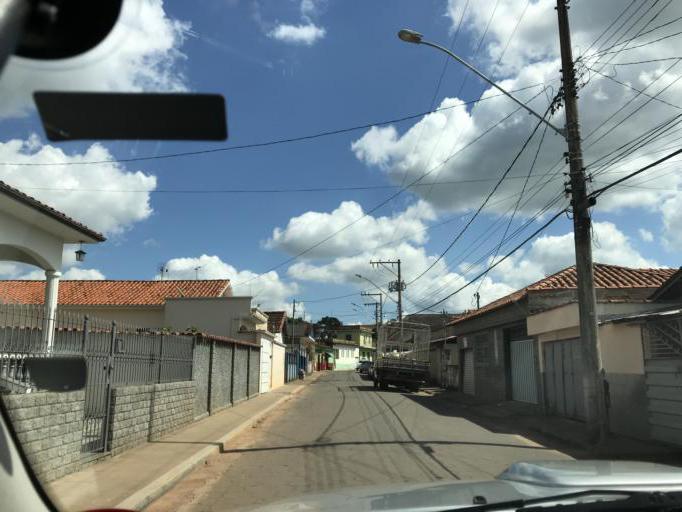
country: BR
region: Minas Gerais
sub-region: Campanha
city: Campanha
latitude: -21.8319
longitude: -45.4087
